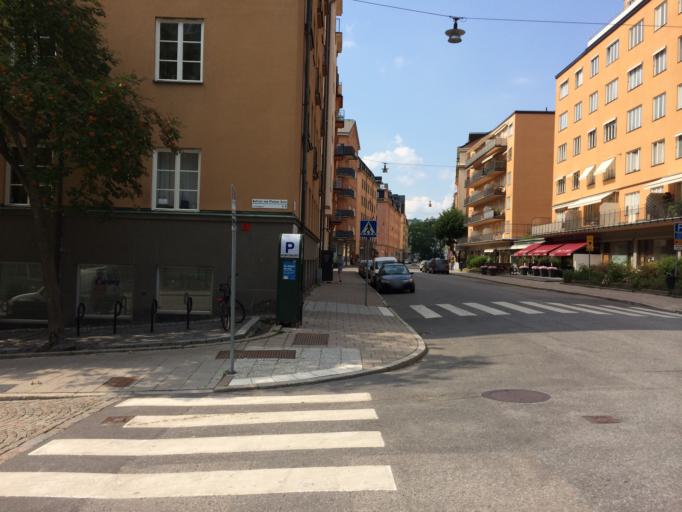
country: SE
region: Stockholm
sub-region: Stockholms Kommun
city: Stockholm
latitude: 59.3291
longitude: 18.0317
